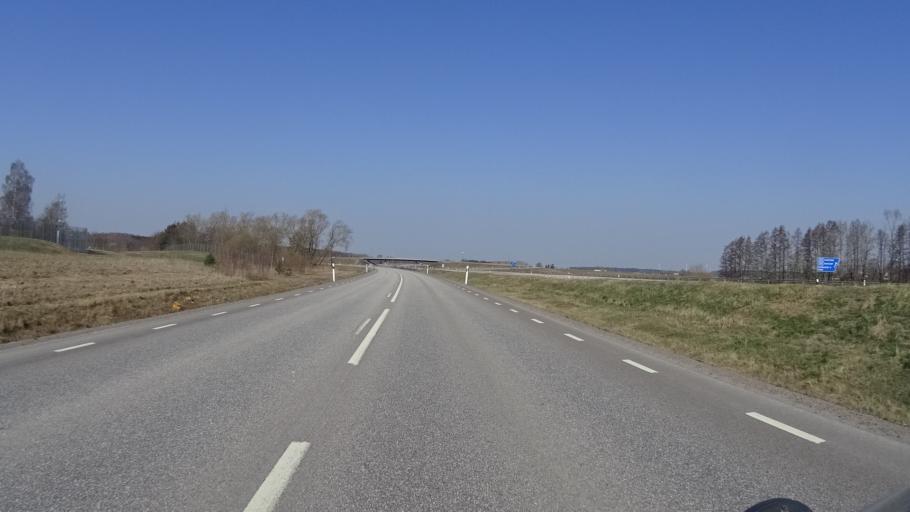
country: SE
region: OEstergoetland
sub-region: Mjolby Kommun
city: Mjolby
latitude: 58.4000
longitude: 15.0980
